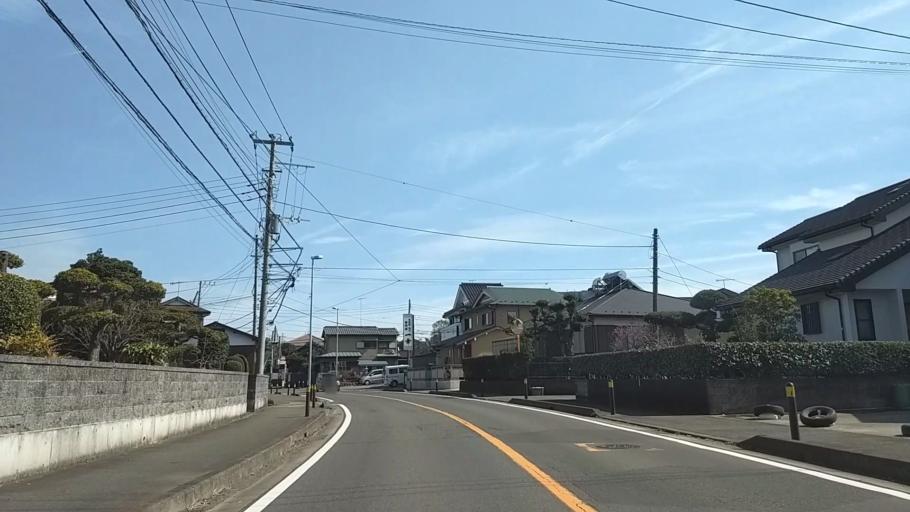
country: JP
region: Kanagawa
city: Chigasaki
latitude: 35.3863
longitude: 139.4113
